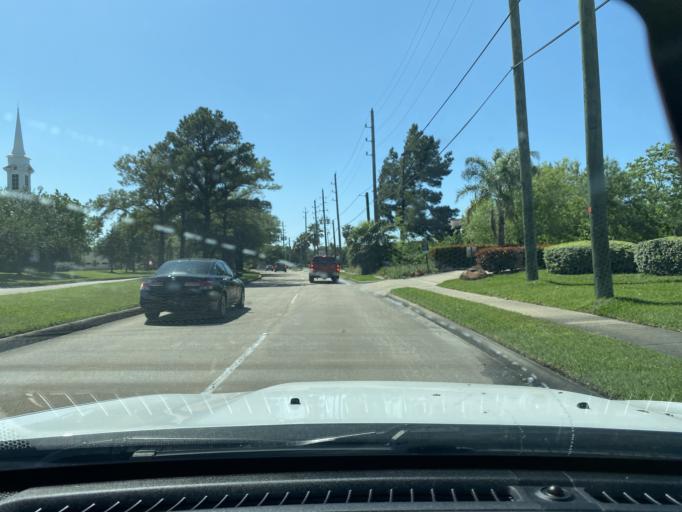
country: US
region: Texas
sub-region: Harris County
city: Jersey Village
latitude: 29.9099
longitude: -95.5669
